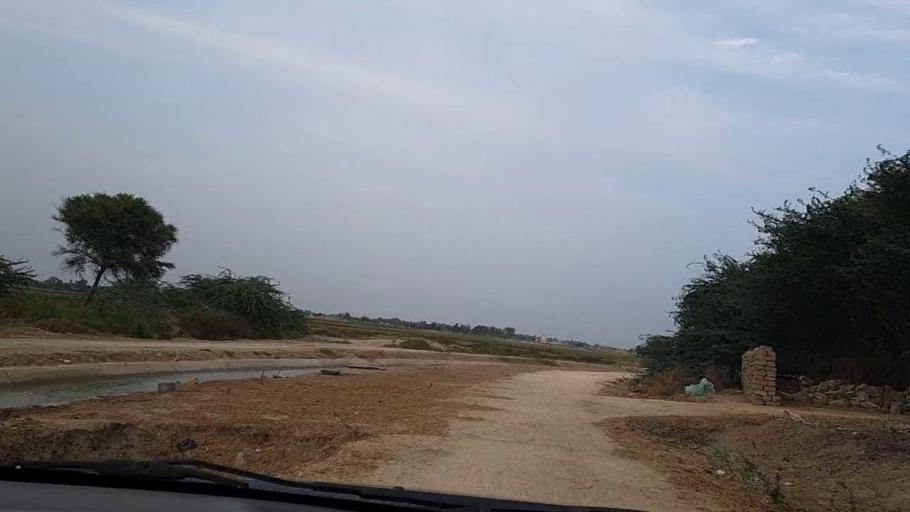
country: PK
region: Sindh
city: Thatta
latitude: 24.7632
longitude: 67.9508
